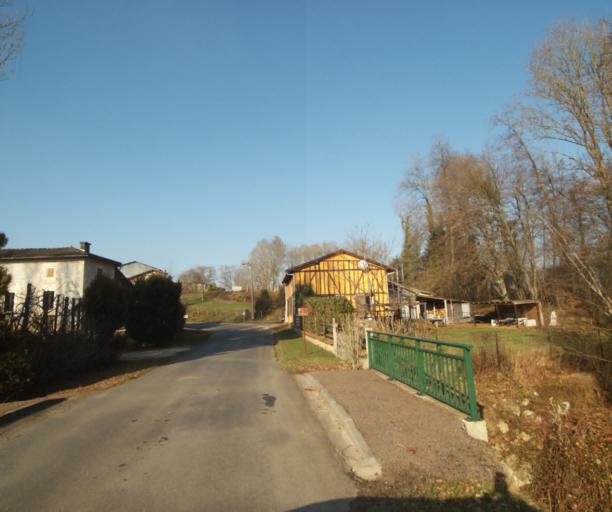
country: FR
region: Champagne-Ardenne
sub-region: Departement de la Haute-Marne
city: Laneuville-a-Remy
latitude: 48.4604
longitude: 4.9202
